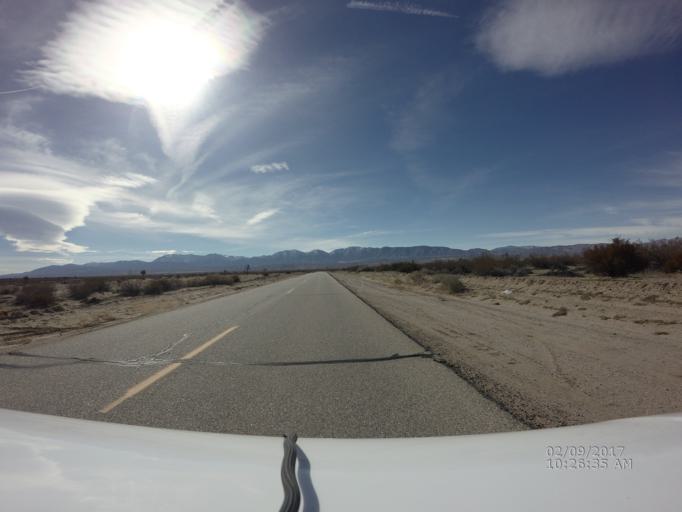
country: US
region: California
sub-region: Los Angeles County
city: Lake Los Angeles
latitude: 34.5467
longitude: -117.8901
